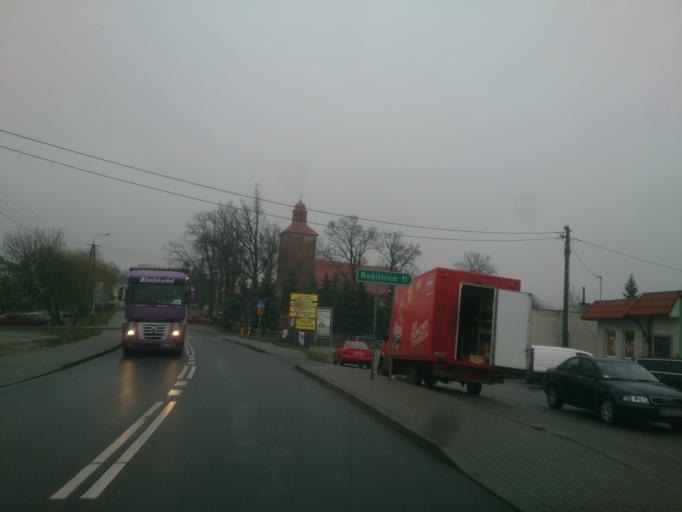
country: PL
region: Kujawsko-Pomorskie
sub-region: Powiat brodnicki
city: Brodnica
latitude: 53.1677
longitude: 19.3876
